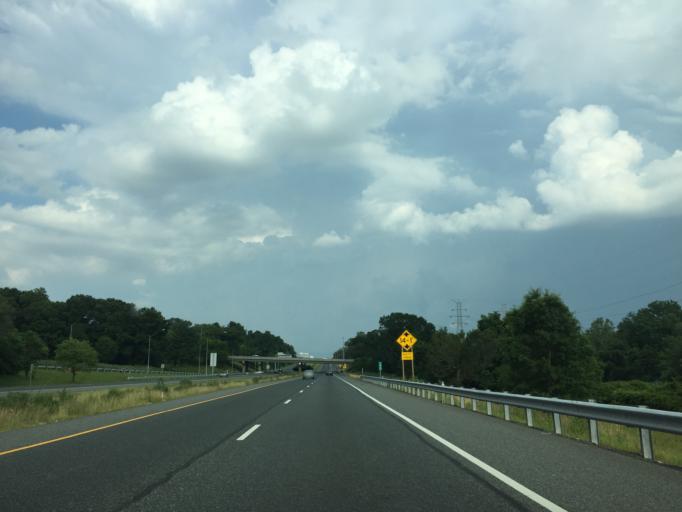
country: US
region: Maryland
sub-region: Baltimore County
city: Lansdowne
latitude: 39.2327
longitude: -76.6535
